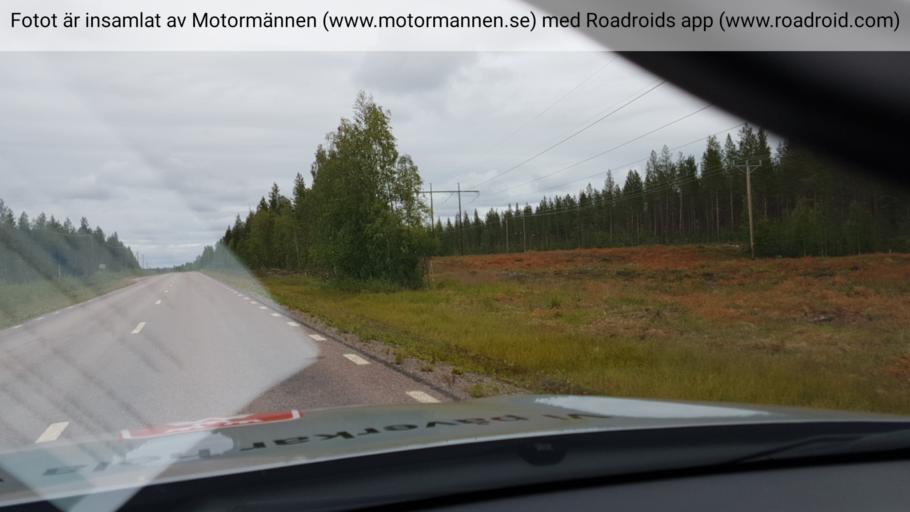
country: SE
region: Norrbotten
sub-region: Pajala Kommun
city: Pajala
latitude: 67.0948
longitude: 22.5741
